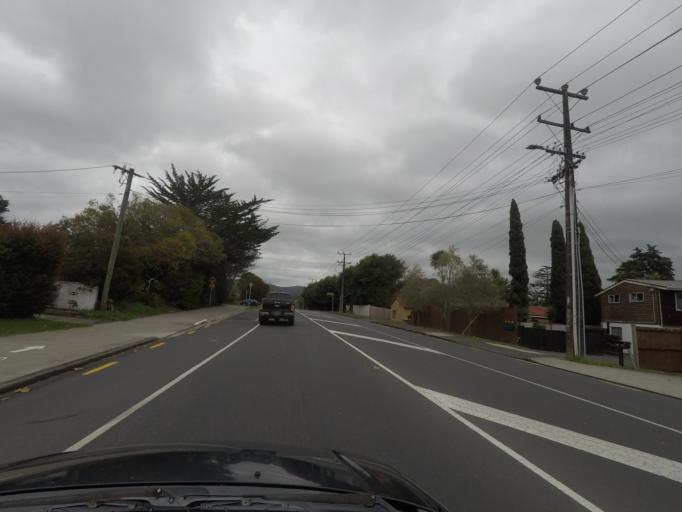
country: NZ
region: Auckland
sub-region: Auckland
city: Waitakere
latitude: -36.9085
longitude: 174.6274
